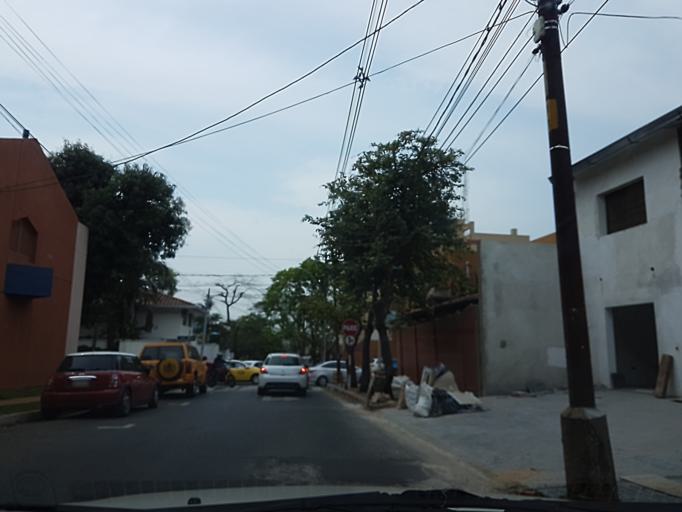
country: PY
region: Central
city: Lambare
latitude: -25.2984
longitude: -57.5803
